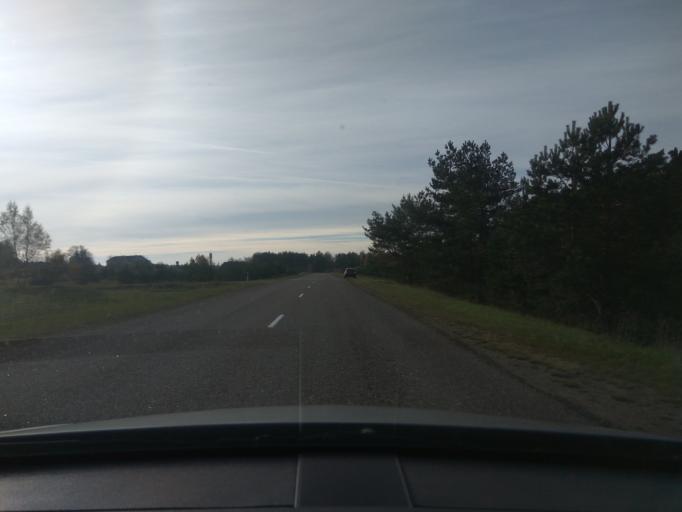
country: LV
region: Alsunga
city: Alsunga
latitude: 57.0103
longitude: 21.3897
